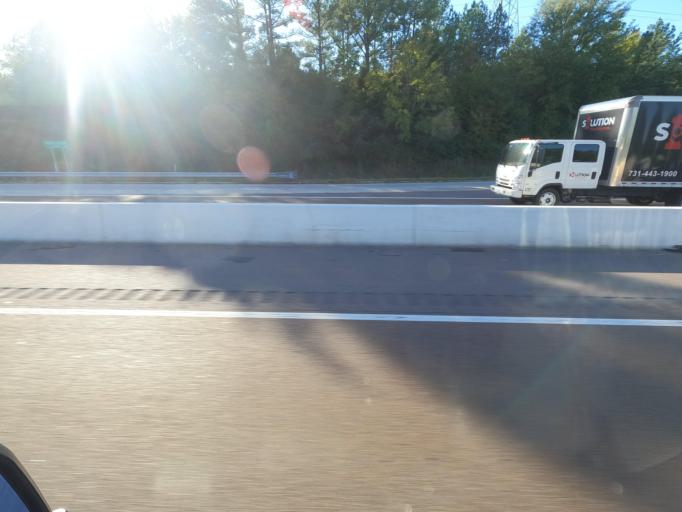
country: US
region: Tennessee
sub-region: Shelby County
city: Germantown
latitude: 35.1287
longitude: -89.8681
